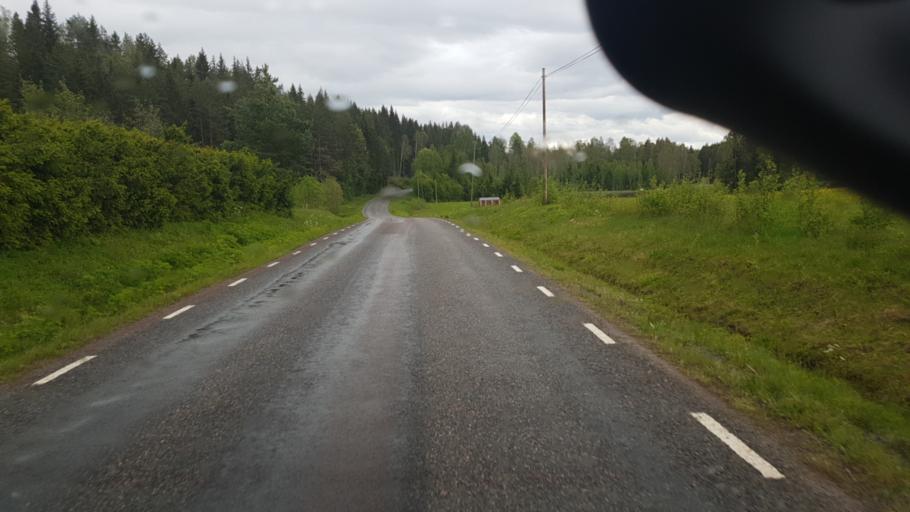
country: SE
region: Vaermland
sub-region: Eda Kommun
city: Amotfors
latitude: 59.8329
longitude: 12.4344
